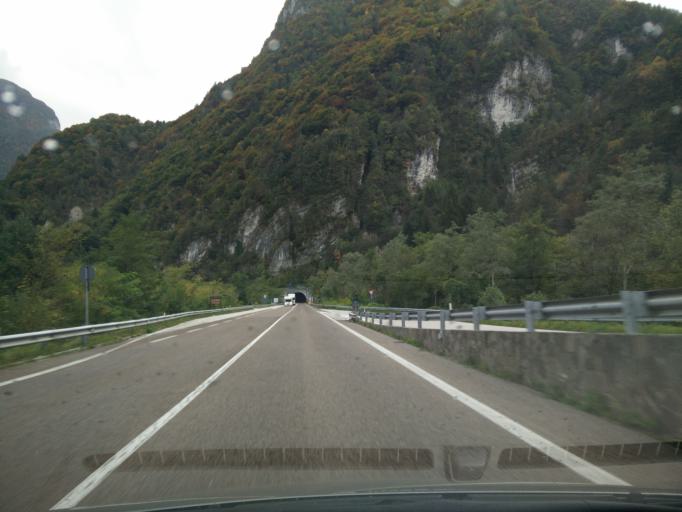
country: IT
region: Veneto
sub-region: Provincia di Belluno
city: Ospitale di Cadore
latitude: 46.3205
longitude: 12.3173
